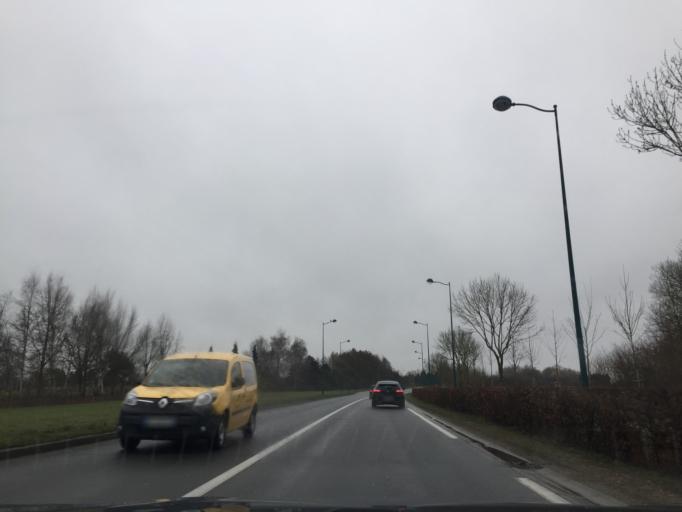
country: FR
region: Ile-de-France
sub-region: Departement de Seine-et-Marne
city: Magny-le-Hongre
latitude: 48.8601
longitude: 2.8061
